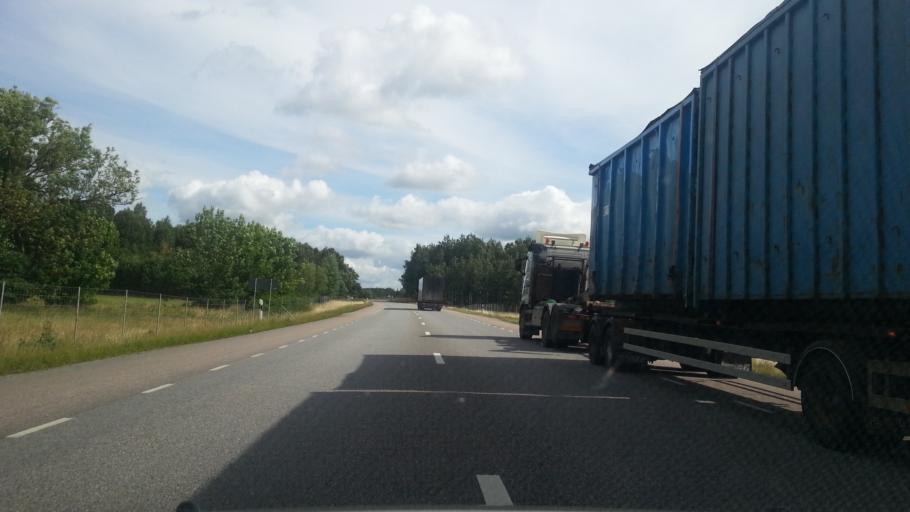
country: SE
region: Vaestra Goetaland
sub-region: Mariestads Kommun
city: Mariestad
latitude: 58.6855
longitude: 13.8481
